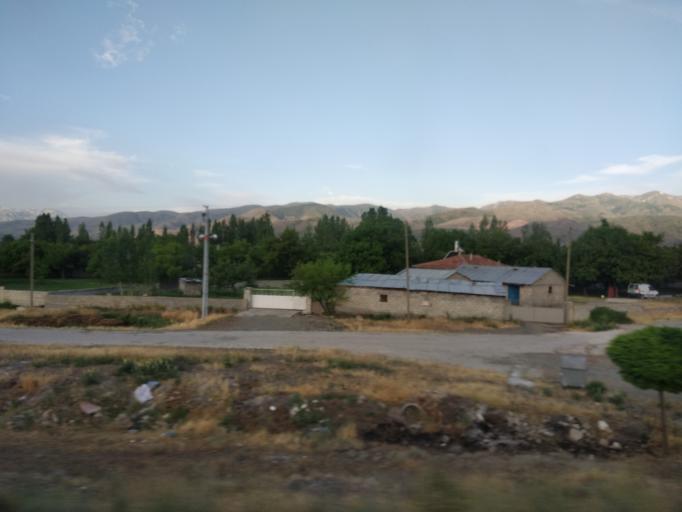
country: TR
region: Erzincan
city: Catalarmut
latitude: 39.8030
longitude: 39.3722
